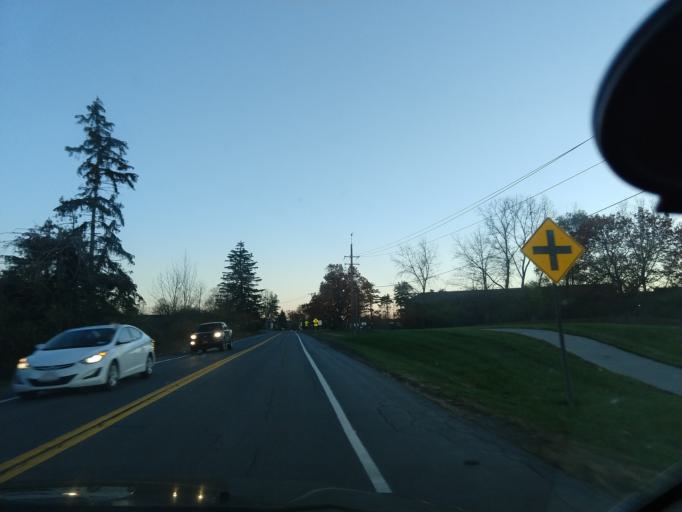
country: US
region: New York
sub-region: Tompkins County
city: Cayuga Heights
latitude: 42.4583
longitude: -76.4748
